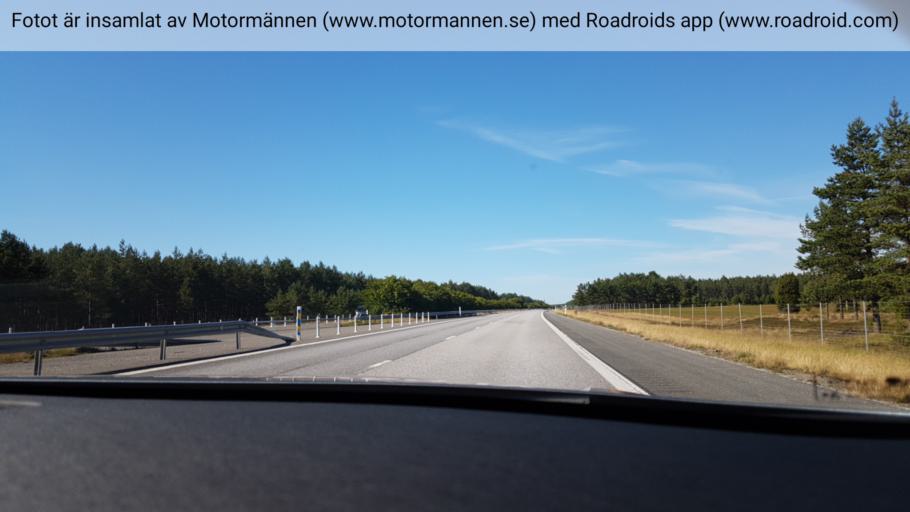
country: SE
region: Joenkoeping
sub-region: Varnamo Kommun
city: Varnamo
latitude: 57.2876
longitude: 14.0849
